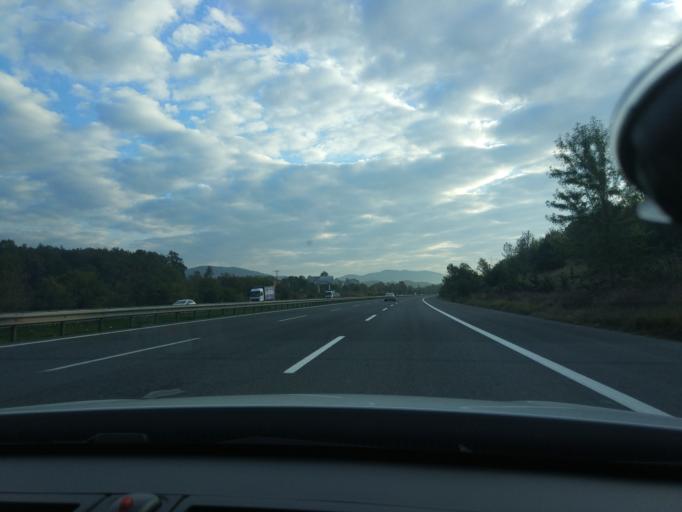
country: TR
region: Sakarya
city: Hendek
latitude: 40.7830
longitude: 30.8061
